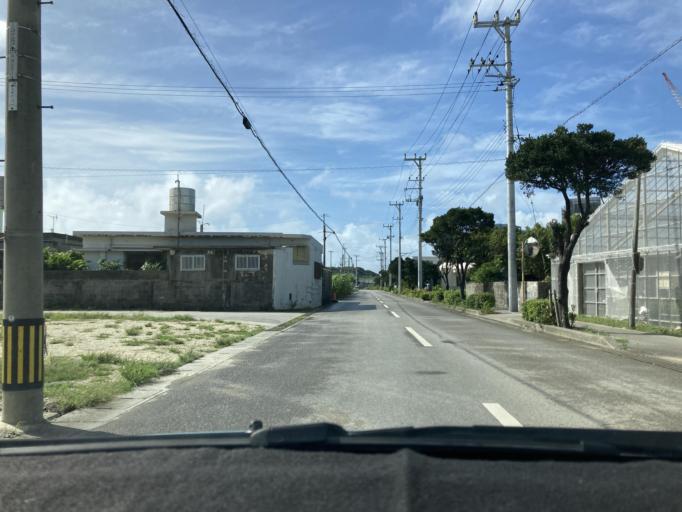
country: JP
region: Okinawa
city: Itoman
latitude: 26.1031
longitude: 127.6622
